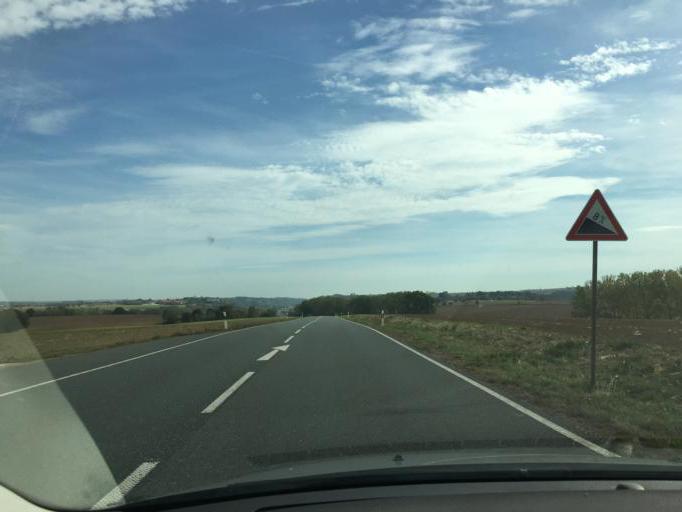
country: DE
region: Saxony
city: Lommatzsch
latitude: 51.2063
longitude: 13.3884
